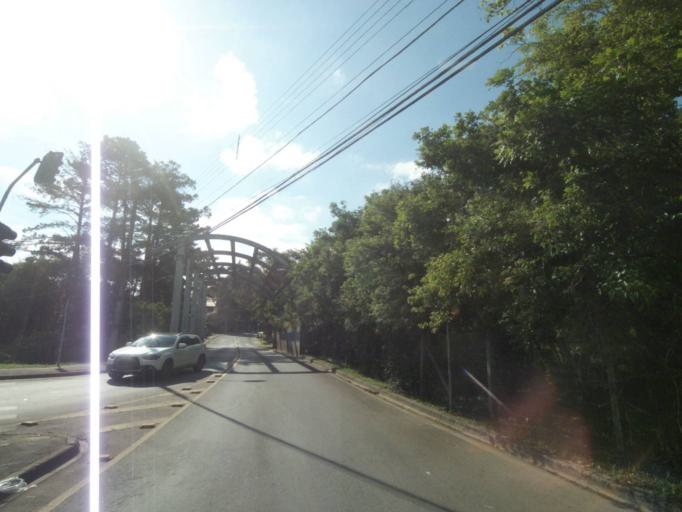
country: BR
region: Parana
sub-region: Curitiba
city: Curitiba
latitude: -25.3871
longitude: -49.3024
